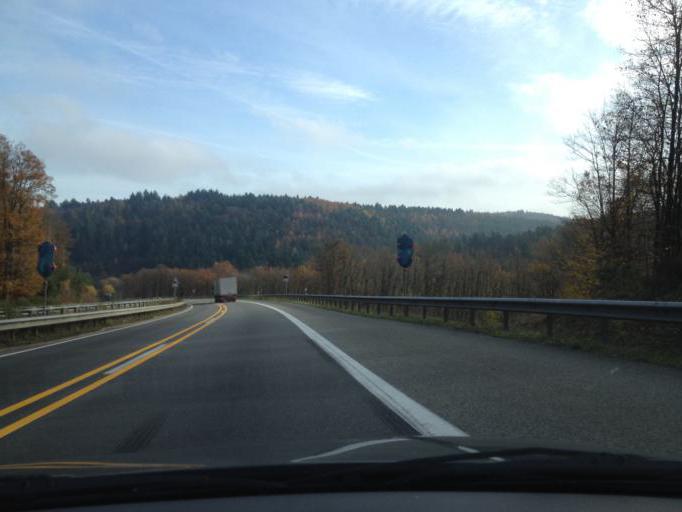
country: DE
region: Rheinland-Pfalz
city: Pirmasens
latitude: 49.2067
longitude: 7.6293
